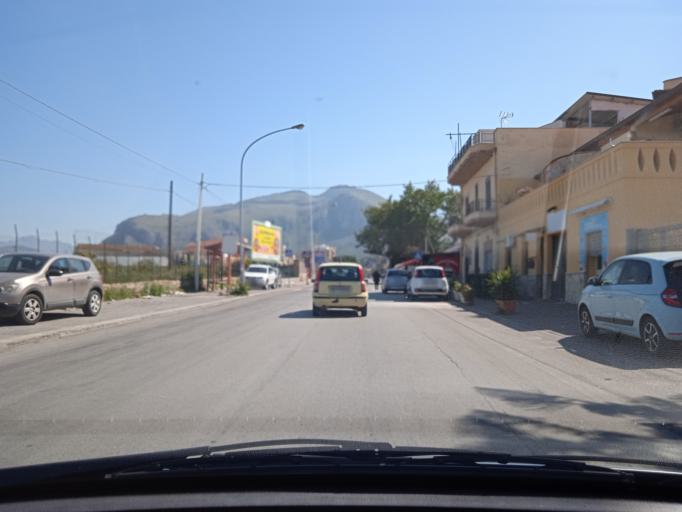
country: IT
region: Sicily
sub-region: Palermo
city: Villabate
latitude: 38.0879
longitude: 13.4329
